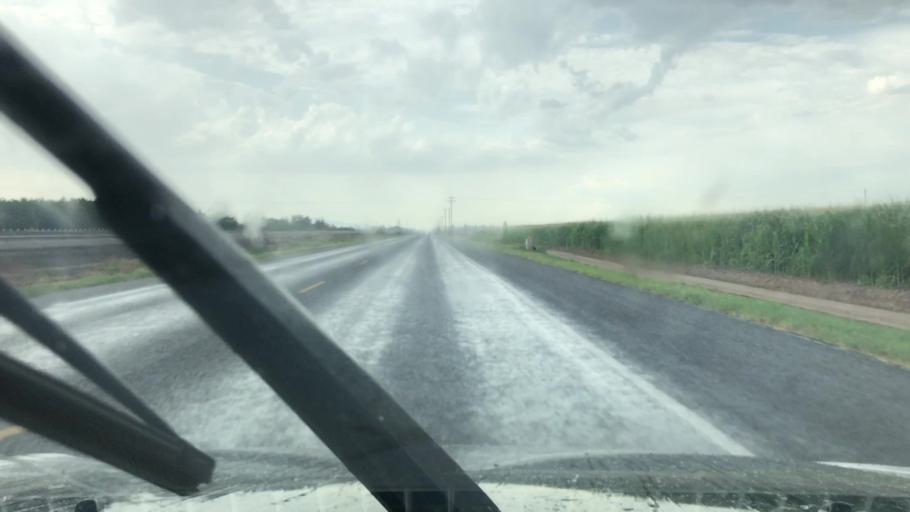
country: US
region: New Mexico
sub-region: Dona Ana County
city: Mesquite
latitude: 32.1509
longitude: -106.6880
